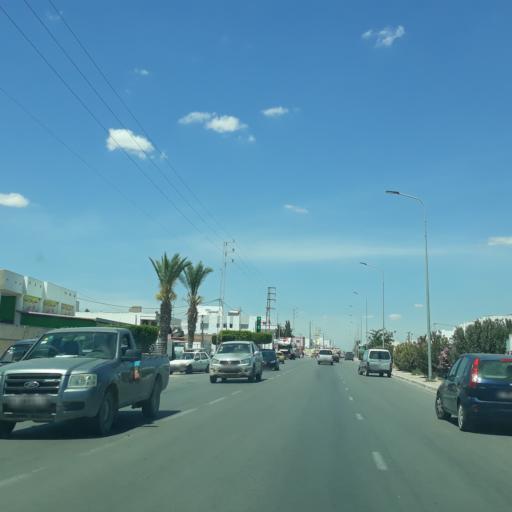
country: TN
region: Safaqis
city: Al Qarmadah
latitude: 34.8095
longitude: 10.7617
